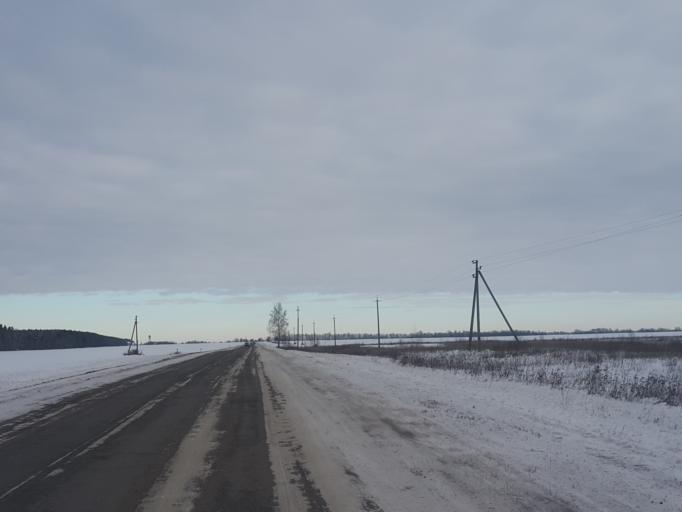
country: RU
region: Tambov
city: Novaya Lyada
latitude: 52.7540
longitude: 41.7198
